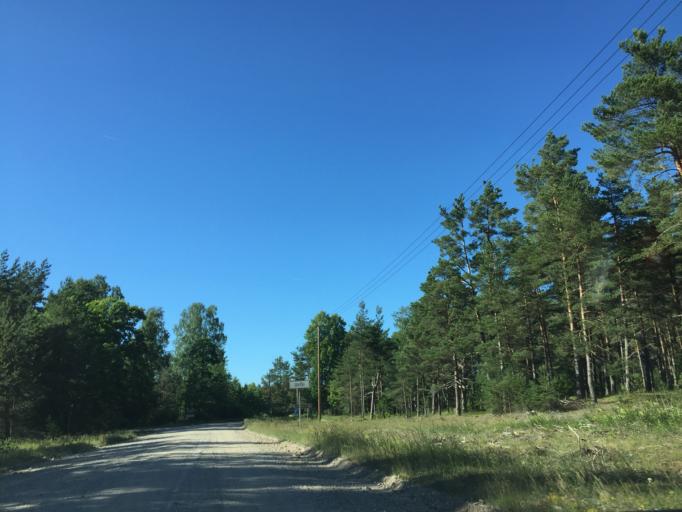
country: LV
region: Ventspils
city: Ventspils
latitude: 57.5691
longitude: 21.7218
